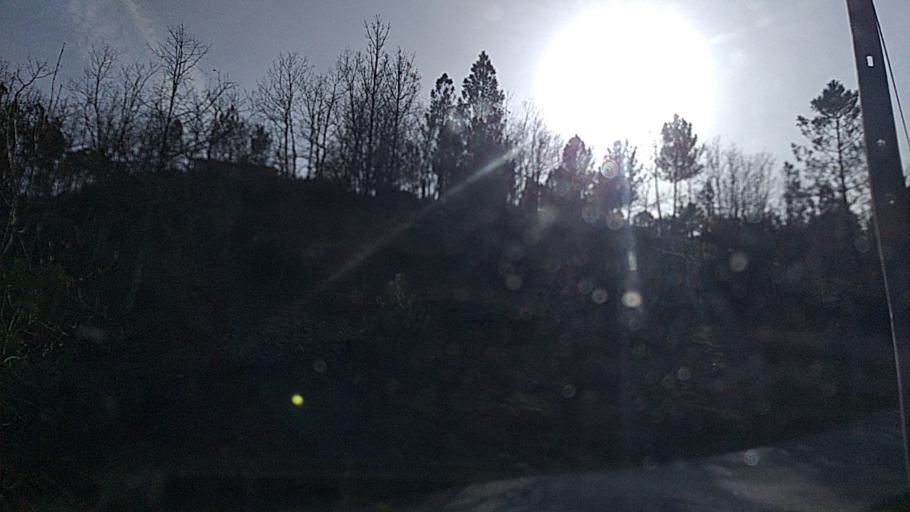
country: PT
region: Guarda
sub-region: Celorico da Beira
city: Celorico da Beira
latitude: 40.6315
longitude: -7.4396
